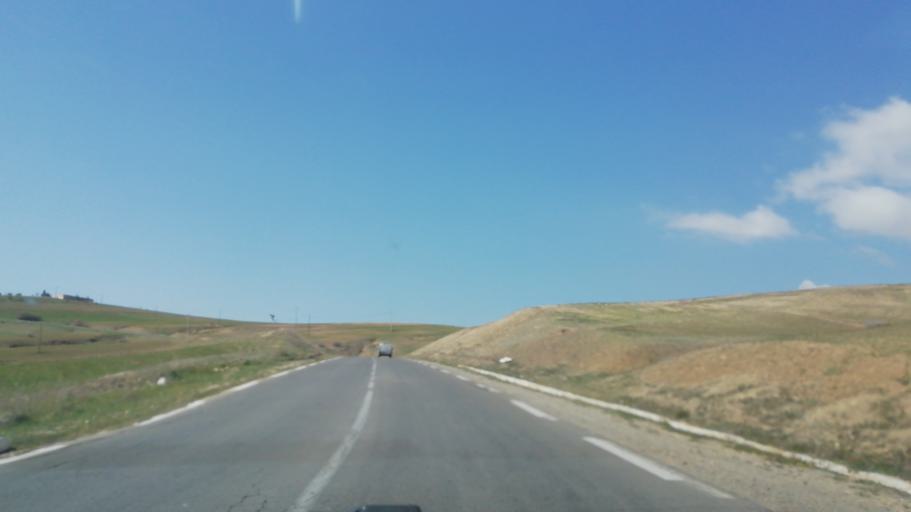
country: DZ
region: Mascara
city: Mascara
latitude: 35.5431
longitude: 0.1118
